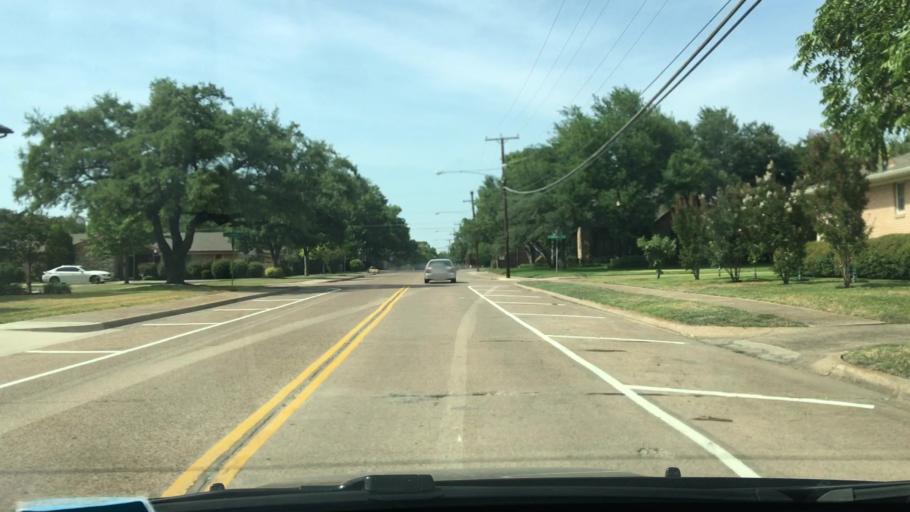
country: US
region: Texas
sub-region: Dallas County
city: Addison
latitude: 32.9122
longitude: -96.8117
